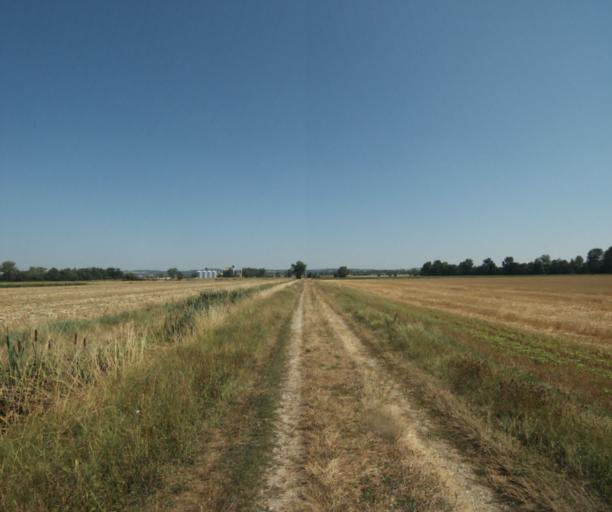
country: FR
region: Midi-Pyrenees
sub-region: Departement de la Haute-Garonne
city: Revel
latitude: 43.5140
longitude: 1.9638
